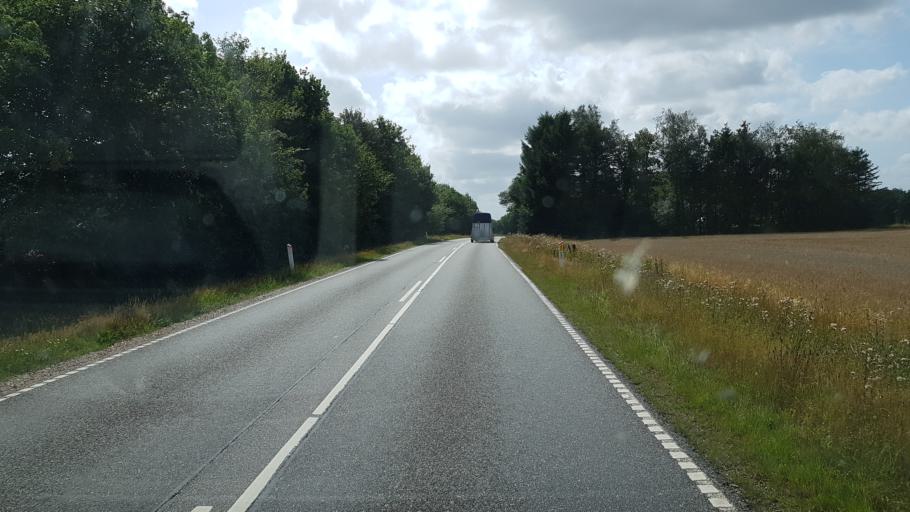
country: DK
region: South Denmark
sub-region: Vejen Kommune
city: Brorup
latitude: 55.5311
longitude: 9.0493
